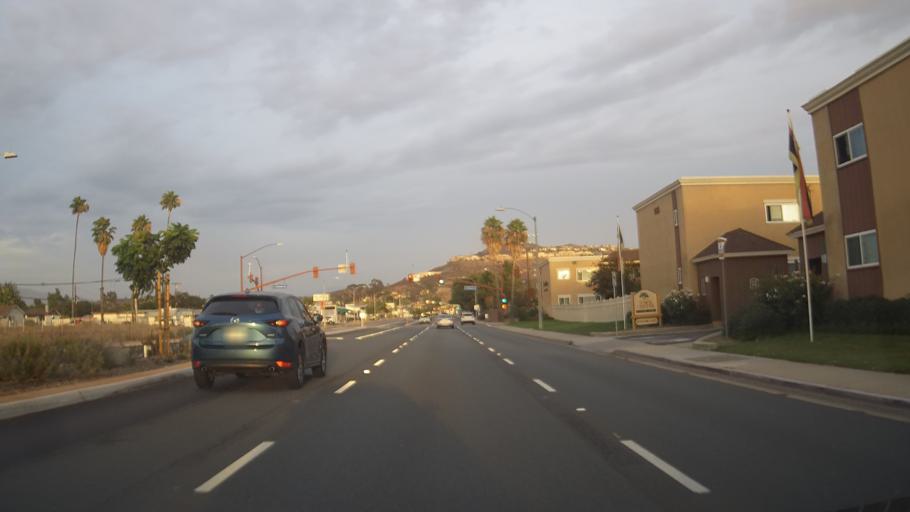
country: US
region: California
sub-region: San Diego County
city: Santee
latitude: 32.8384
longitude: -116.9748
